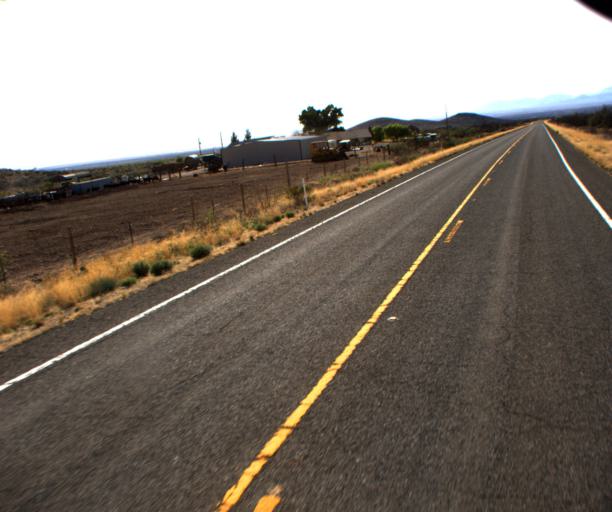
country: US
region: Arizona
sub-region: Cochise County
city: Willcox
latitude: 32.1822
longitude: -109.6625
